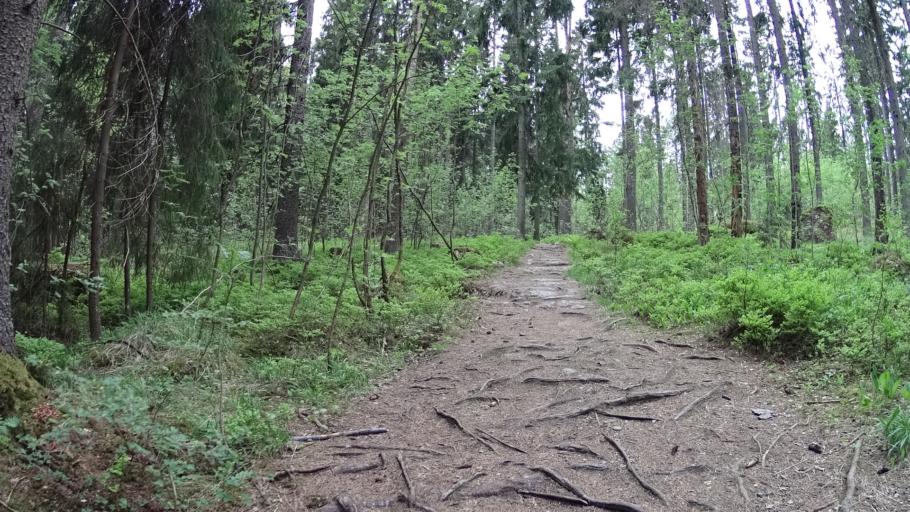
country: FI
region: Uusimaa
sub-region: Helsinki
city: Kilo
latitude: 60.2466
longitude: 24.7936
